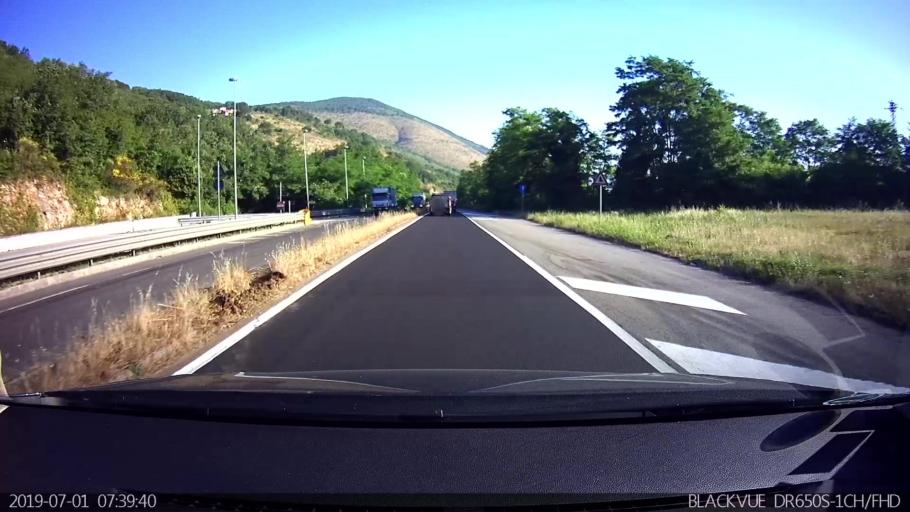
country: IT
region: Latium
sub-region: Provincia di Frosinone
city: Giuliano di Roma
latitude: 41.5513
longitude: 13.2678
